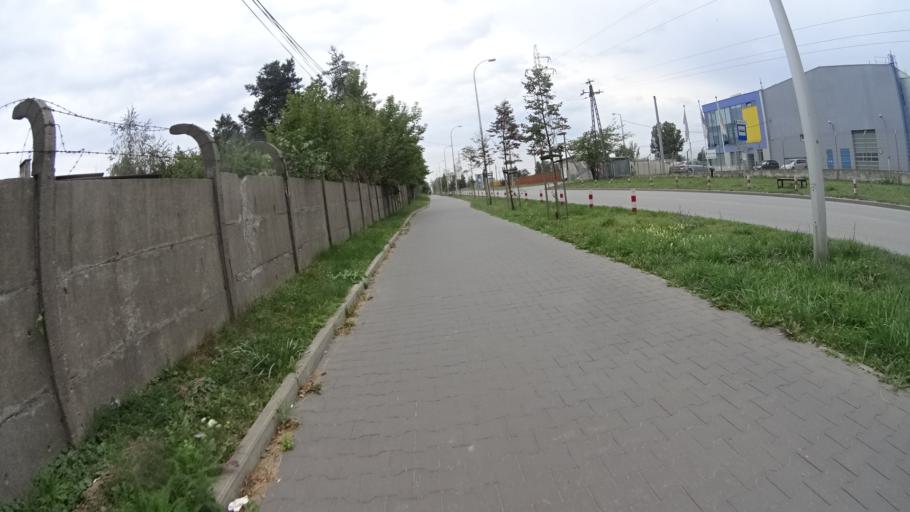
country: PL
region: Masovian Voivodeship
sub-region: Powiat pruszkowski
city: Otrebusy
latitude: 52.1634
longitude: 20.7671
